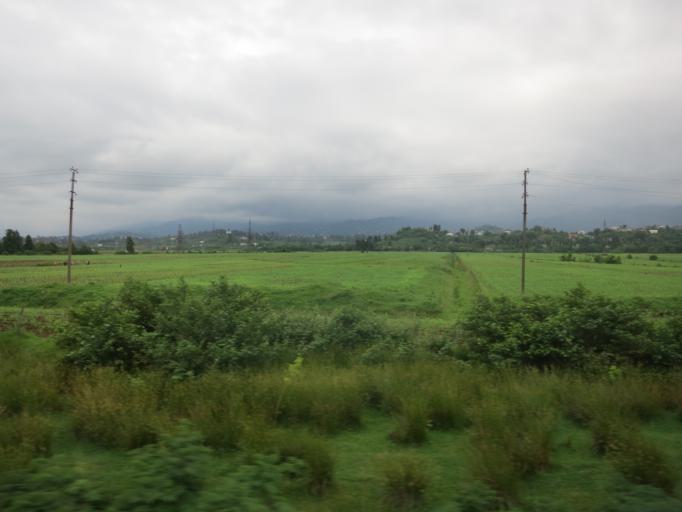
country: GE
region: Ajaria
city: Kobuleti
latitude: 41.7921
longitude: 41.7693
